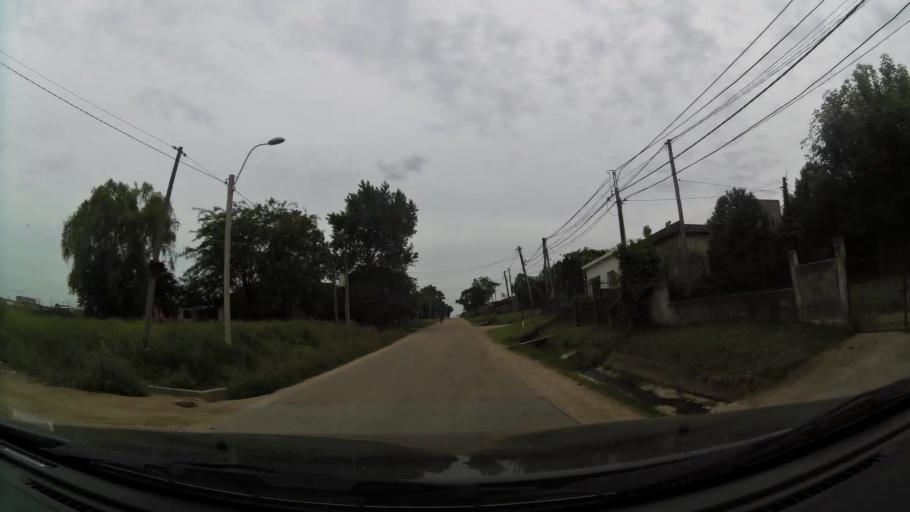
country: UY
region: Canelones
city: Las Piedras
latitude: -34.7186
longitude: -56.2037
